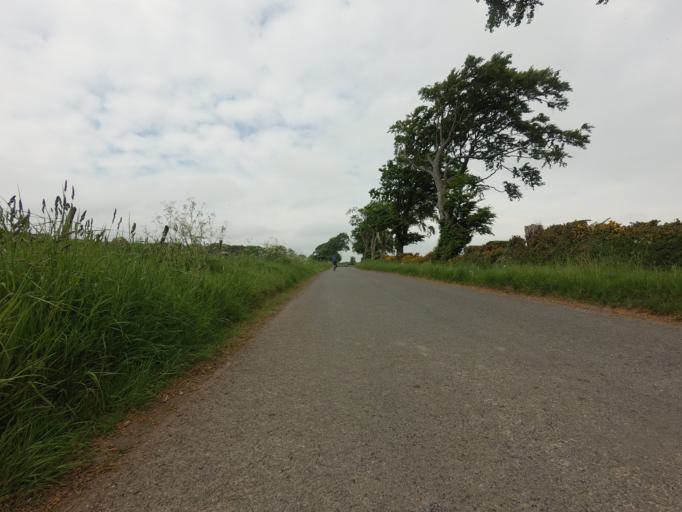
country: GB
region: Scotland
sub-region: Perth and Kinross
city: Kinross
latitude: 56.1795
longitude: -3.4383
